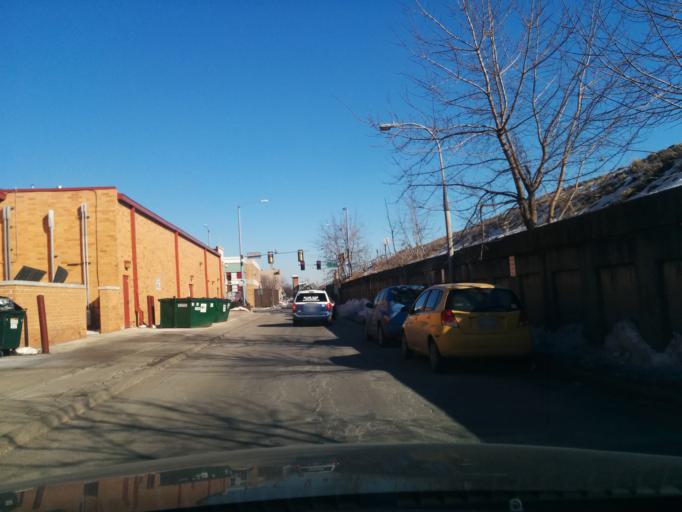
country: US
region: Illinois
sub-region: Cook County
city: Forest Park
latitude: 41.8871
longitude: -87.8059
